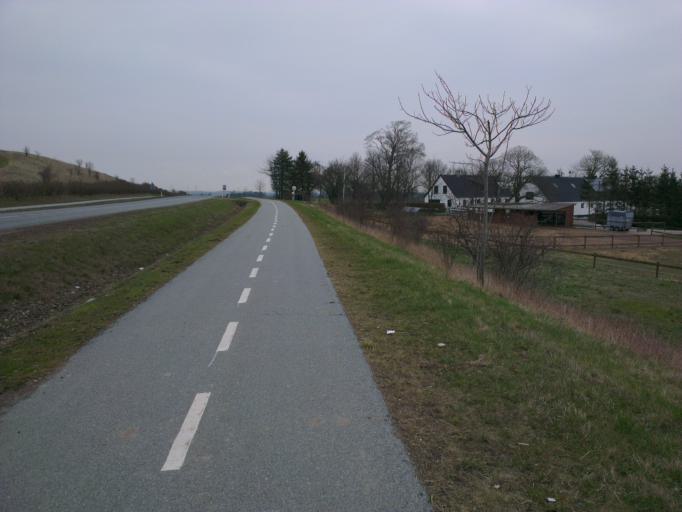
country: DK
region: Capital Region
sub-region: Frederikssund Kommune
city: Skibby
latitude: 55.7771
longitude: 11.9636
